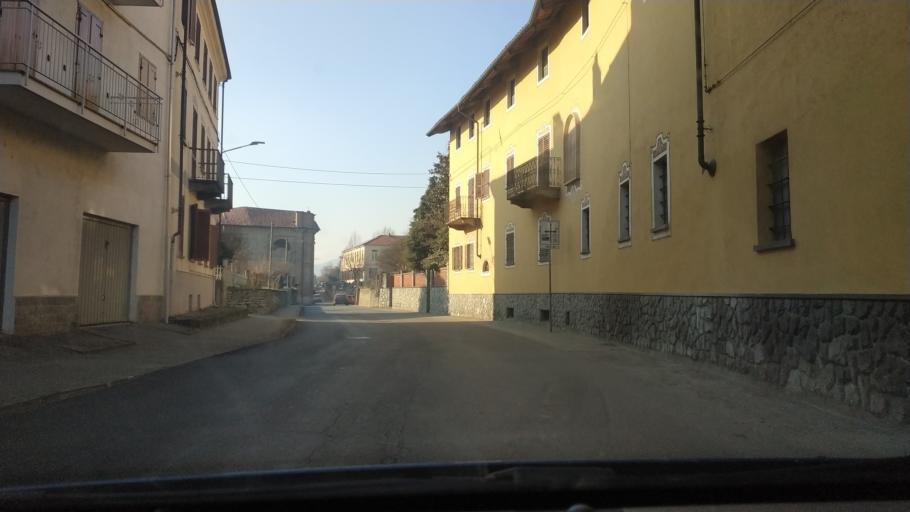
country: IT
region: Piedmont
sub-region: Provincia di Torino
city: Pavone Canavese
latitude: 45.4343
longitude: 7.8562
